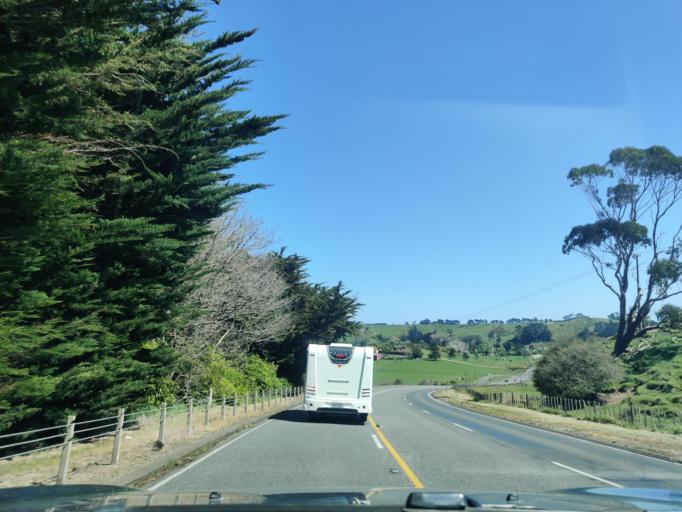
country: NZ
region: Taranaki
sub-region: South Taranaki District
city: Patea
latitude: -39.8108
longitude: 174.7430
